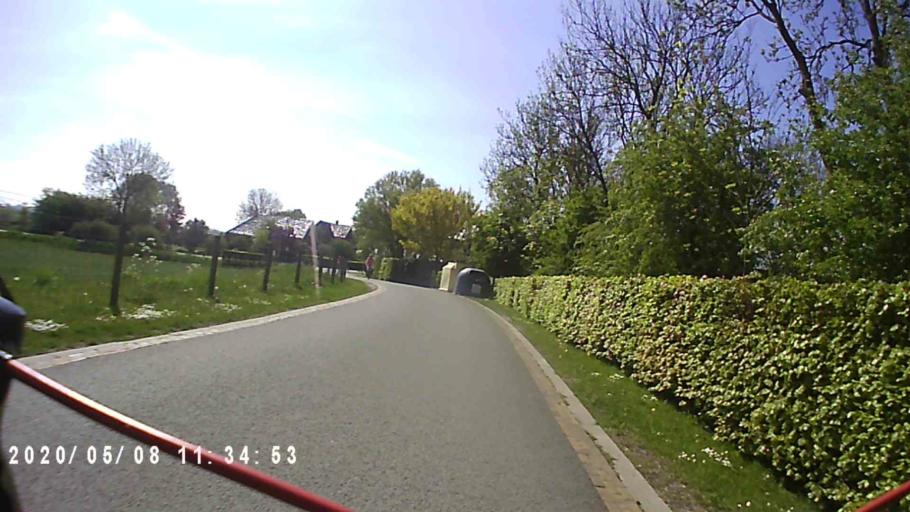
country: NL
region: Groningen
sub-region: Gemeente Bedum
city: Bedum
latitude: 53.3425
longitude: 6.7112
